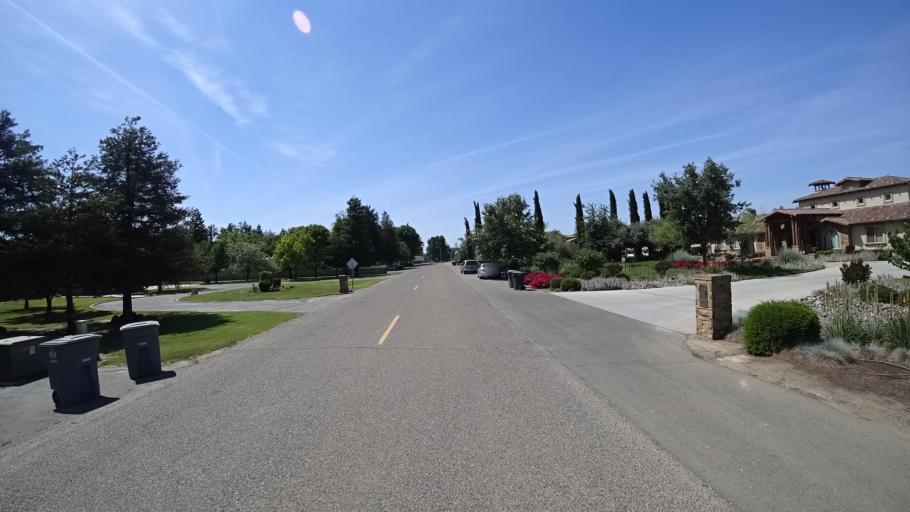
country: US
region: California
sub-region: Kings County
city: Armona
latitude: 36.3412
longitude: -119.7045
